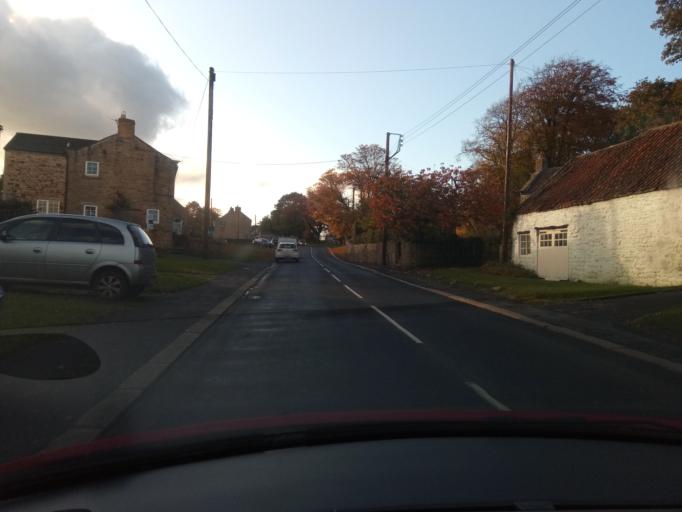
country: GB
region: England
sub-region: County Durham
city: Hamsterley
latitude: 54.6747
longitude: -1.8213
